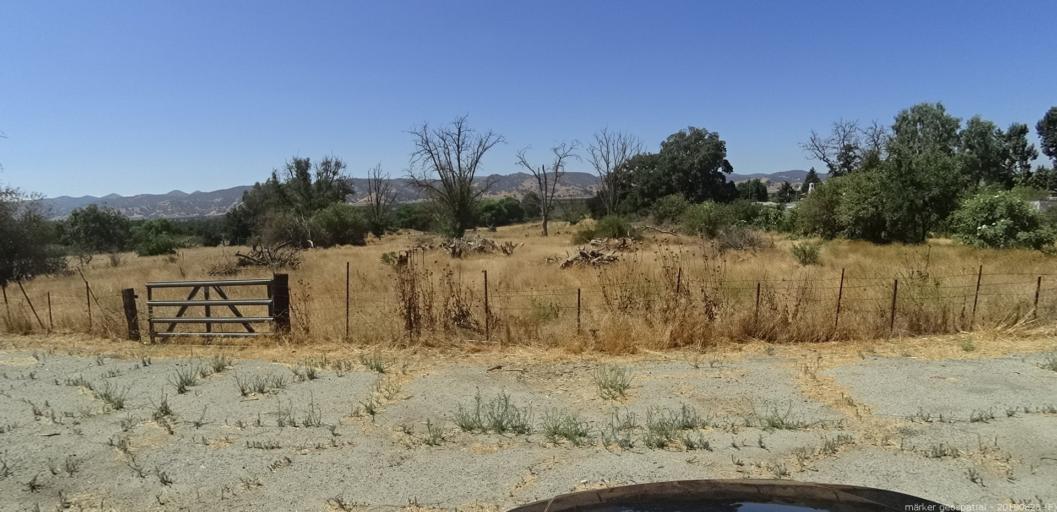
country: US
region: California
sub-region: San Luis Obispo County
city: Lake Nacimiento
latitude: 36.0184
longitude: -120.9038
